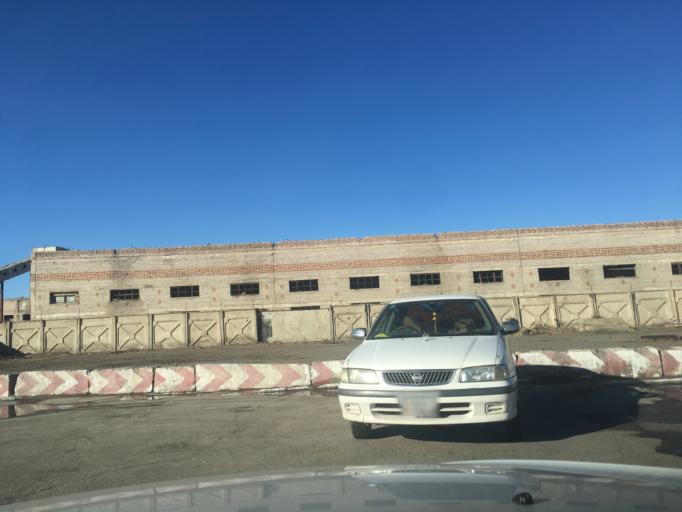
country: MN
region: Ulaanbaatar
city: Ulaanbaatar
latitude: 47.9033
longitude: 106.7765
